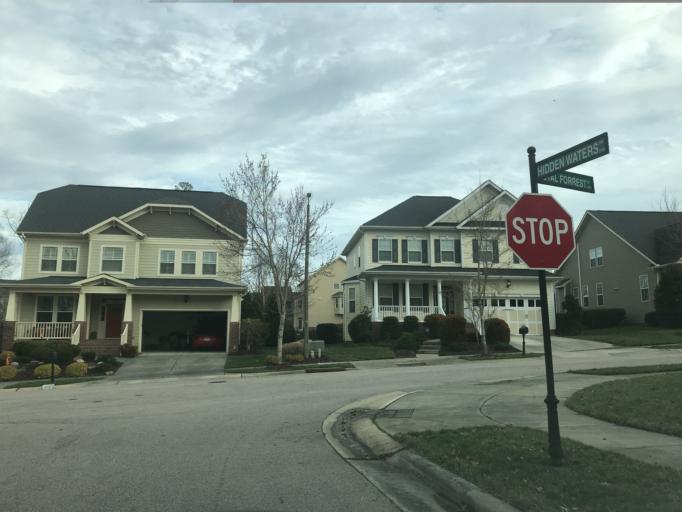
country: US
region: North Carolina
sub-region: Wake County
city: Wake Forest
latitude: 35.9318
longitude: -78.5684
